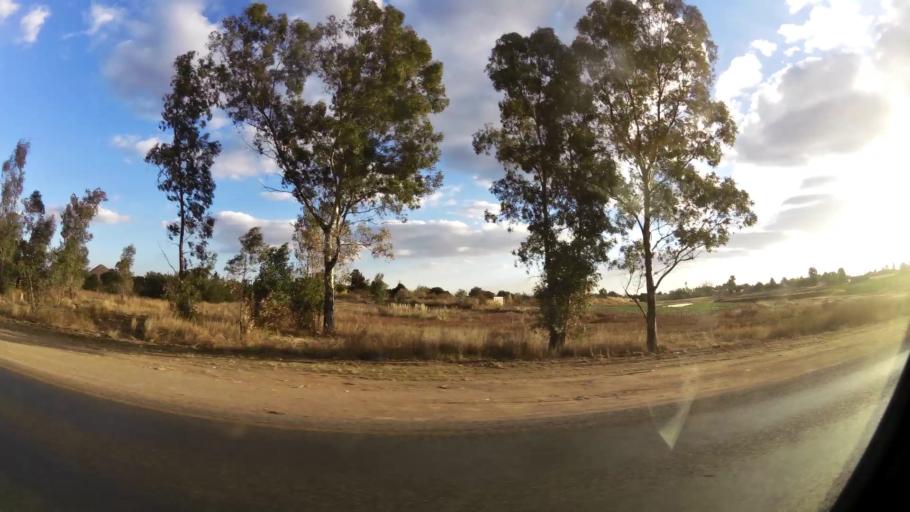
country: ZA
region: Gauteng
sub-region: Ekurhuleni Metropolitan Municipality
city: Tembisa
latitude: -25.9520
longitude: 28.1825
